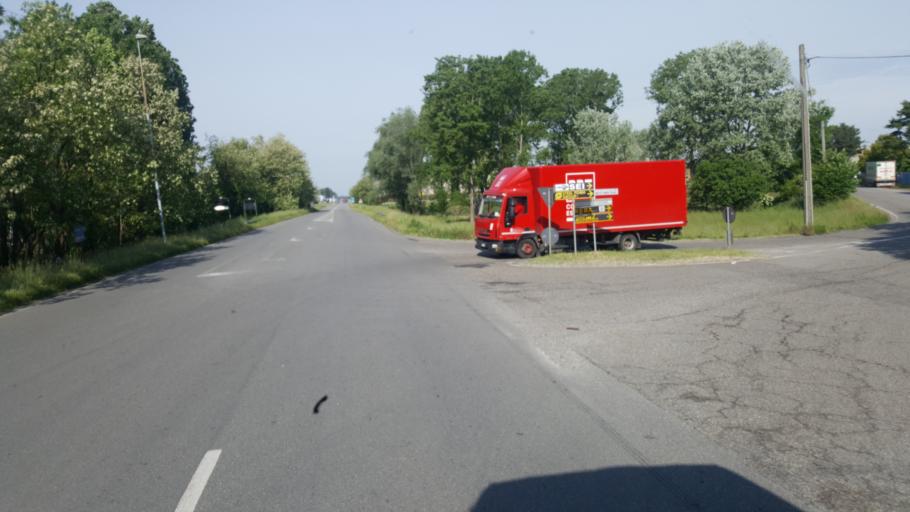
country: IT
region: Lombardy
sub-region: Citta metropolitana di Milano
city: Liscate
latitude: 45.4838
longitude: 9.3928
